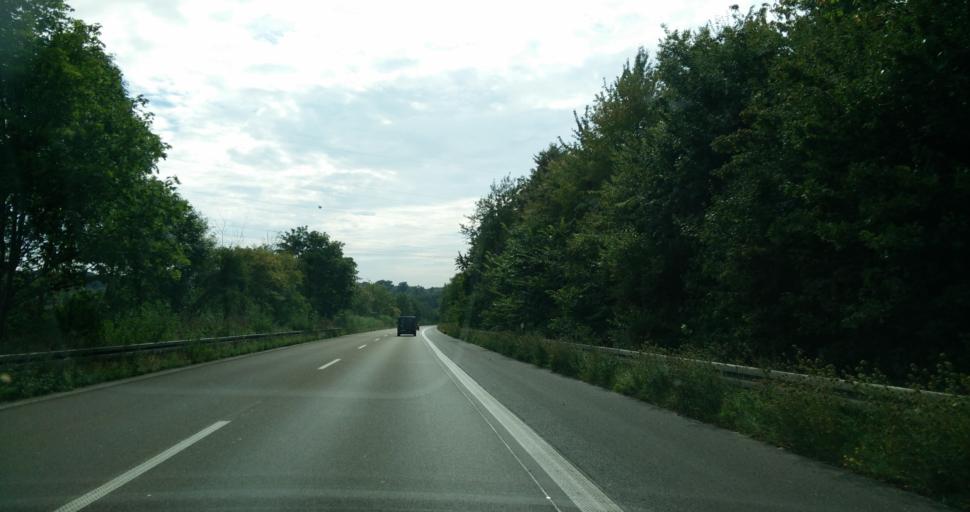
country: DE
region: North Rhine-Westphalia
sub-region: Regierungsbezirk Dusseldorf
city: Ratingen
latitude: 51.2814
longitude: 6.8584
